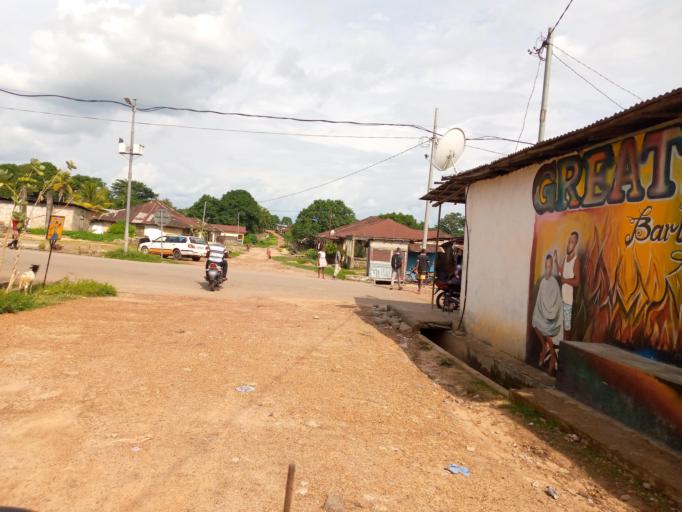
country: SL
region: Northern Province
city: Magburaka
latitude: 8.7249
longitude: -11.9487
